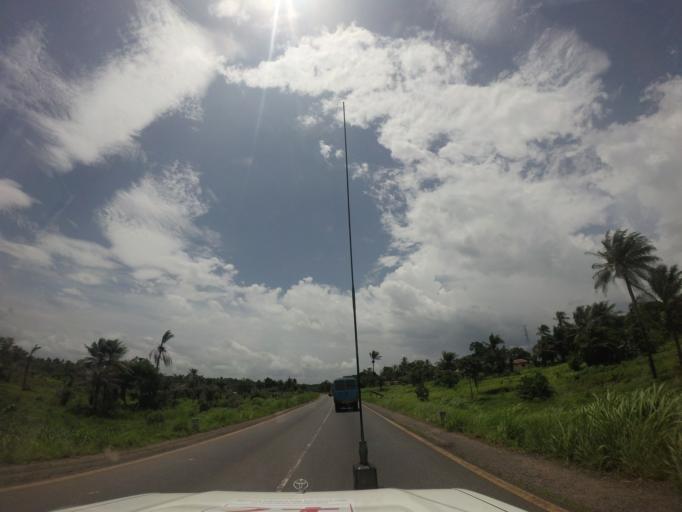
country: SL
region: Western Area
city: Waterloo
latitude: 8.3643
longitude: -12.9632
